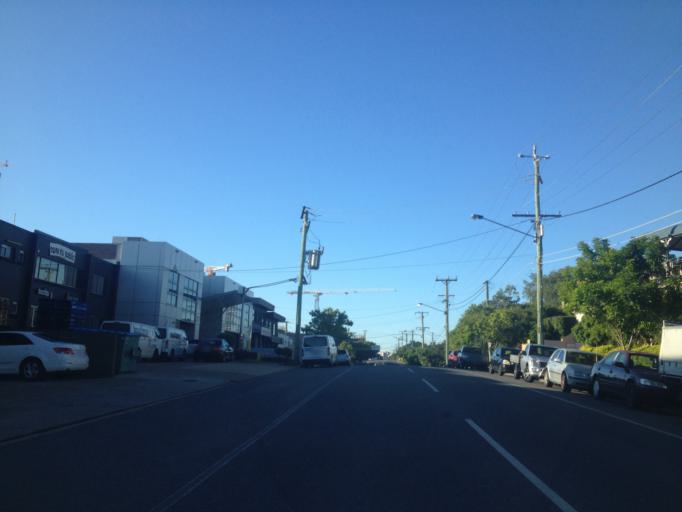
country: AU
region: Queensland
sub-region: Brisbane
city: Toowong
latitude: -27.4846
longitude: 153.0024
